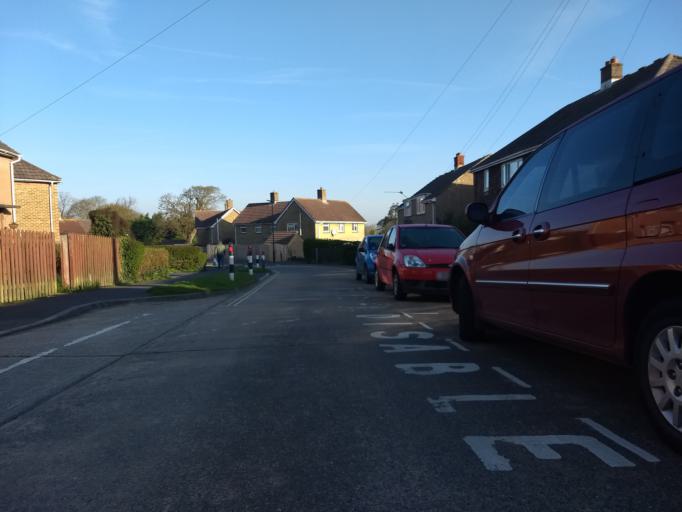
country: GB
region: England
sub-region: Isle of Wight
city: Ryde
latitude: 50.7275
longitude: -1.1771
